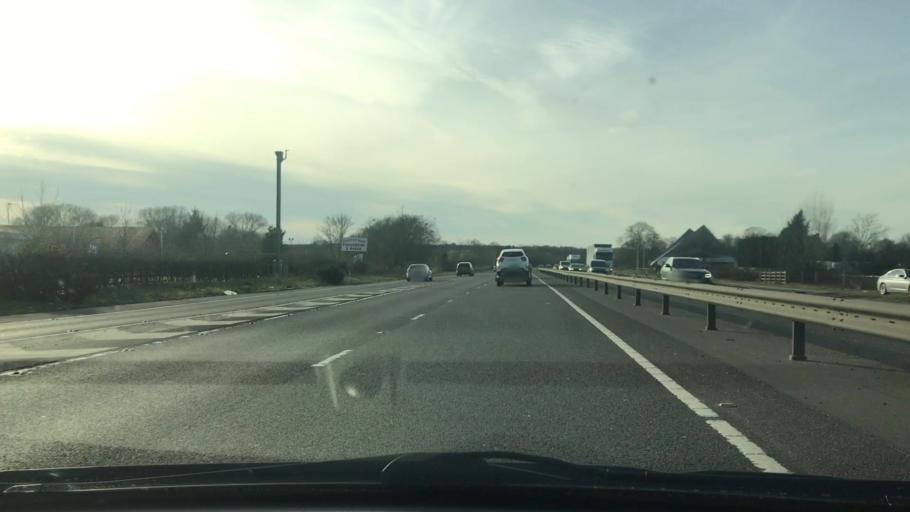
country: GB
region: England
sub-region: Nottinghamshire
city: Tuxford
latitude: 53.2557
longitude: -0.9250
